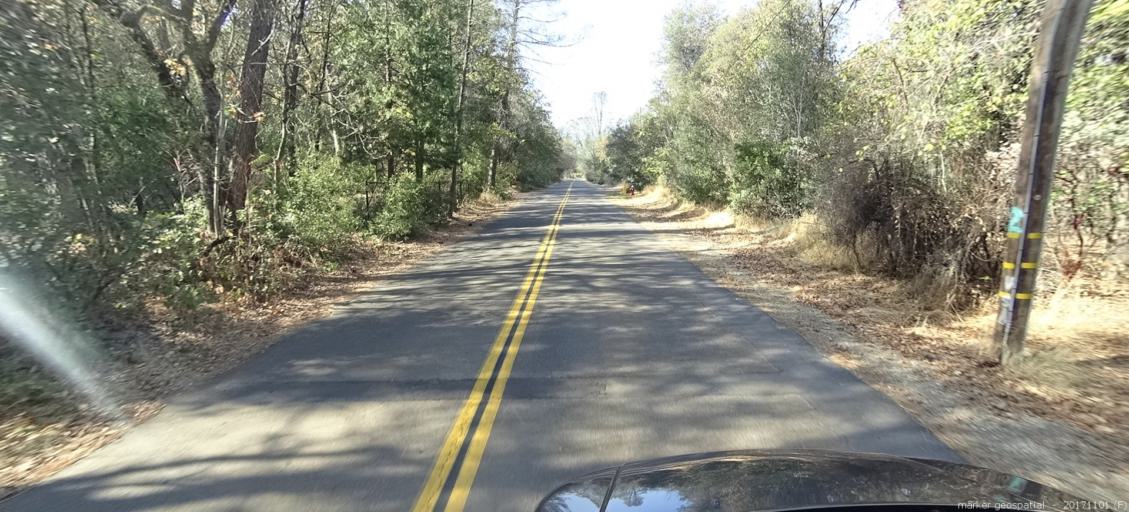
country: US
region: California
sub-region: Shasta County
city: Central Valley (historical)
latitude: 40.6774
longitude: -122.4090
